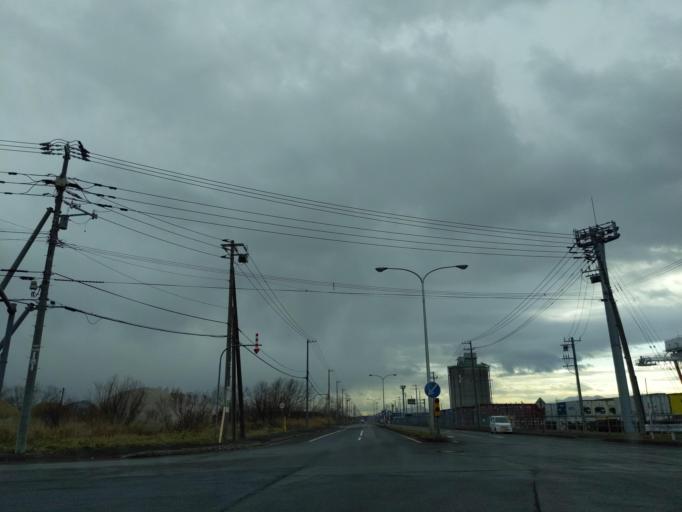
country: JP
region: Hokkaido
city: Ishikari
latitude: 43.1938
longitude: 141.2941
